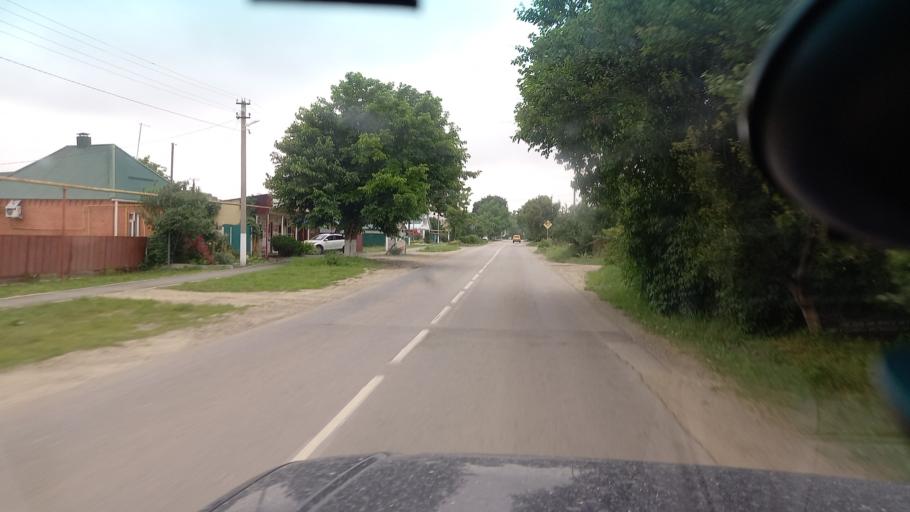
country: RU
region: Krasnodarskiy
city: Mostovskoy
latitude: 44.4134
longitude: 40.7825
